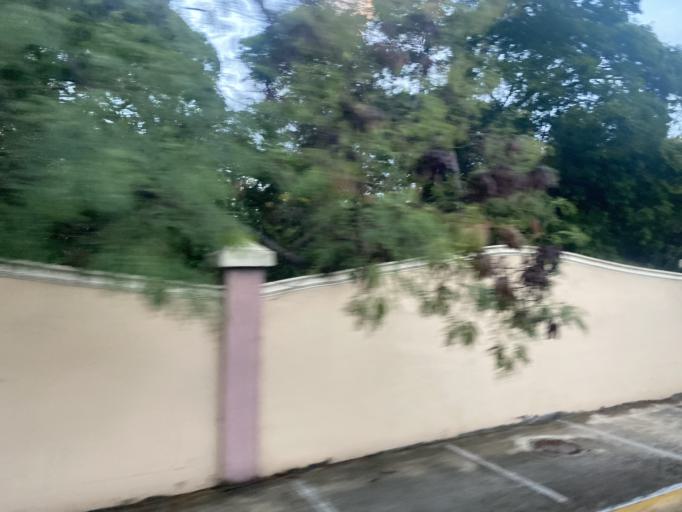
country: DO
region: San Juan
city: Punta Cana
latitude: 18.7110
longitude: -68.4611
